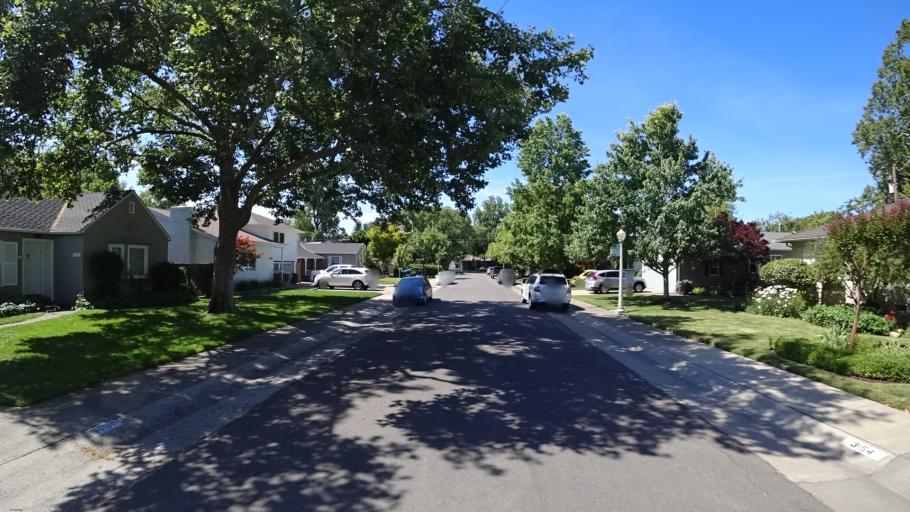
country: US
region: California
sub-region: Sacramento County
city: Sacramento
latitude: 38.5493
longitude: -121.4980
